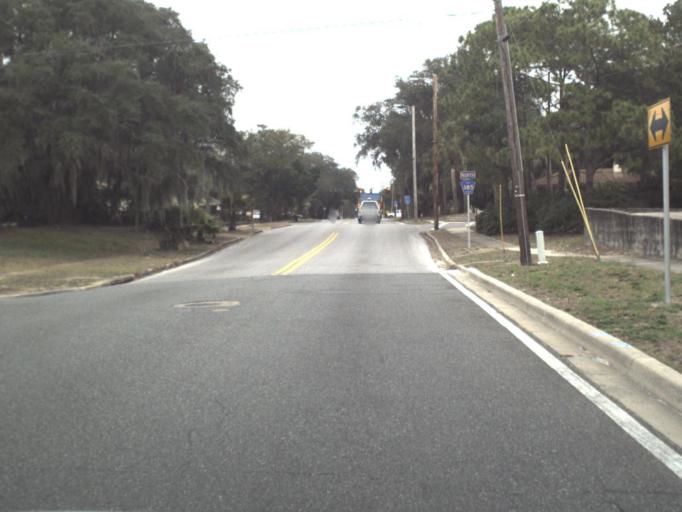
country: US
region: Florida
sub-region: Bay County
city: Pretty Bayou
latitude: 30.1664
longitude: -85.6921
